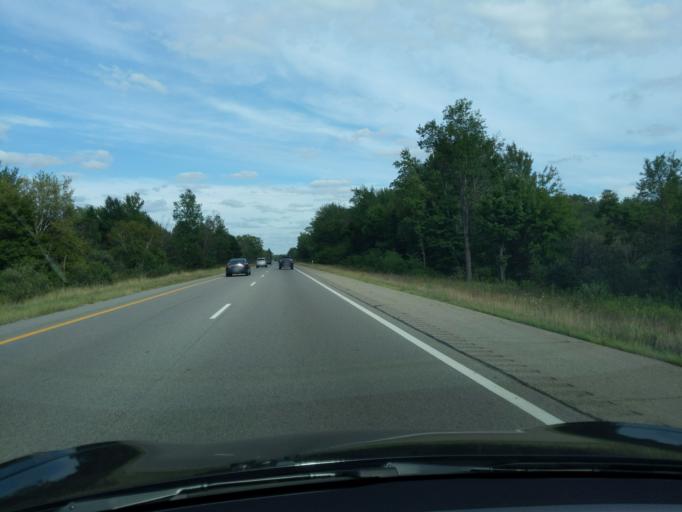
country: US
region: Michigan
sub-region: Ottawa County
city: Coopersville
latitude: 43.0699
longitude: -86.0035
